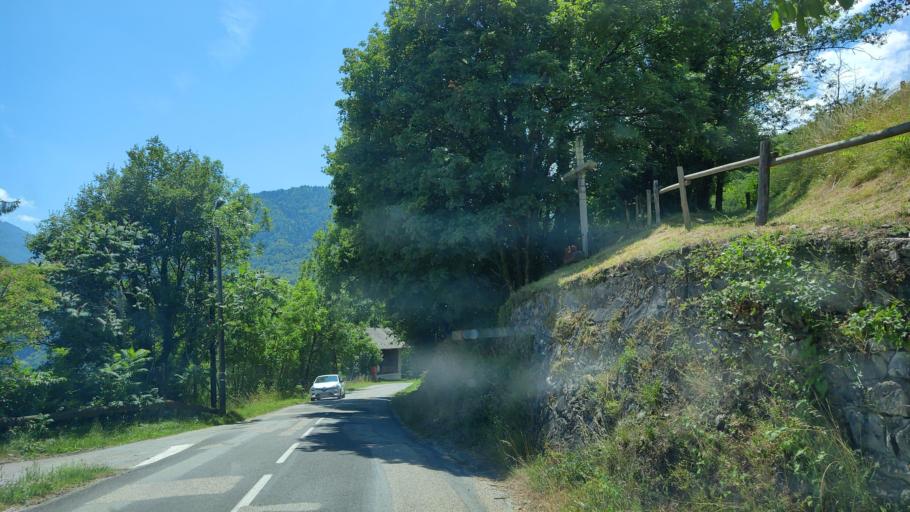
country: FR
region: Rhone-Alpes
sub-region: Departement de la Savoie
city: Aiton
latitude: 45.4816
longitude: 6.2787
